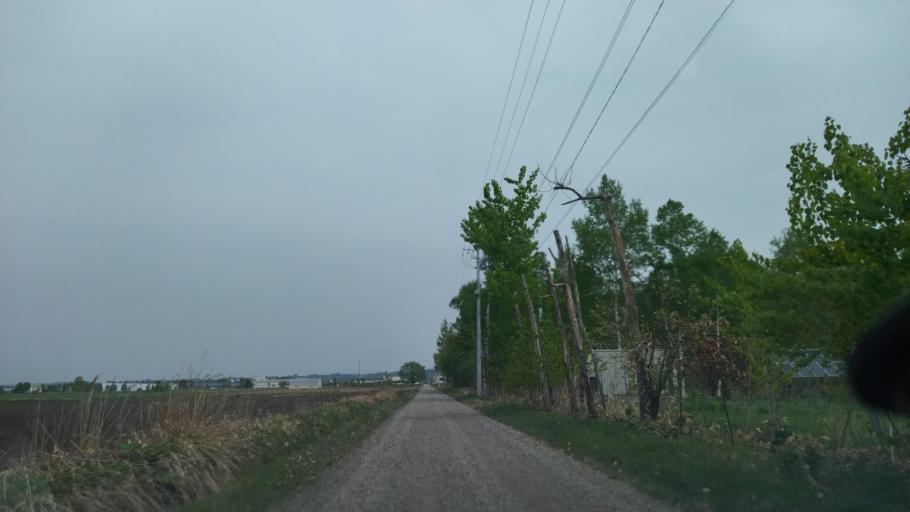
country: JP
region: Hokkaido
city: Obihiro
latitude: 42.9155
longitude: 143.0970
